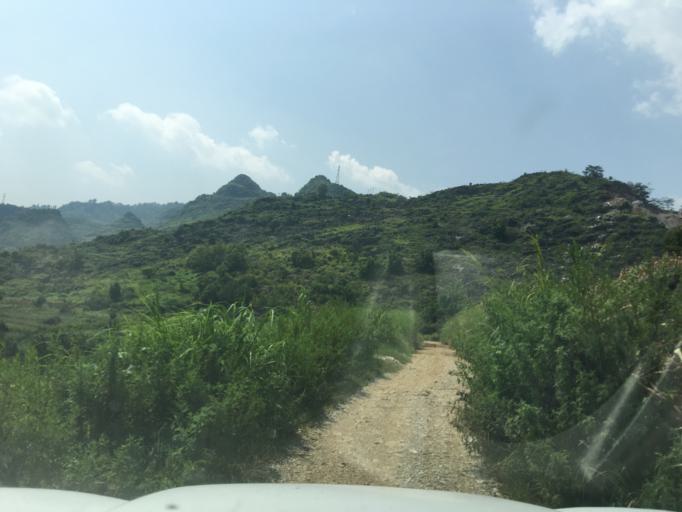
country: CN
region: Guangxi Zhuangzu Zizhiqu
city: Xinzhou
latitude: 24.9950
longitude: 105.7523
